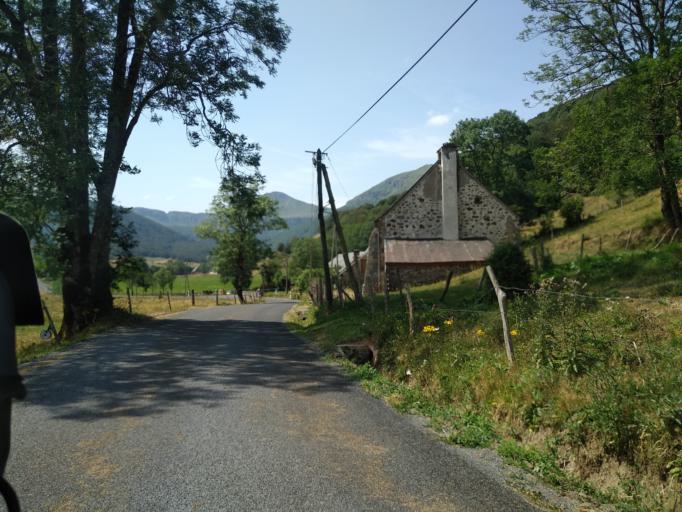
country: FR
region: Auvergne
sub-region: Departement du Cantal
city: Riom-es-Montagnes
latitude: 45.1484
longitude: 2.6986
